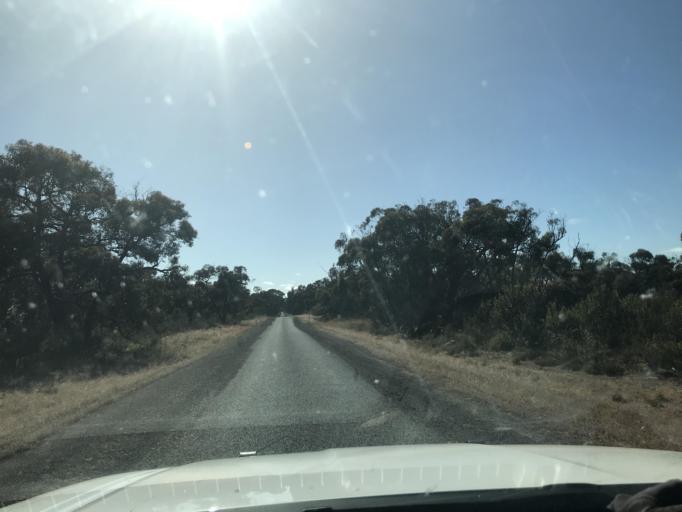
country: AU
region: Victoria
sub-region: Horsham
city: Horsham
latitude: -37.0239
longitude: 141.6923
